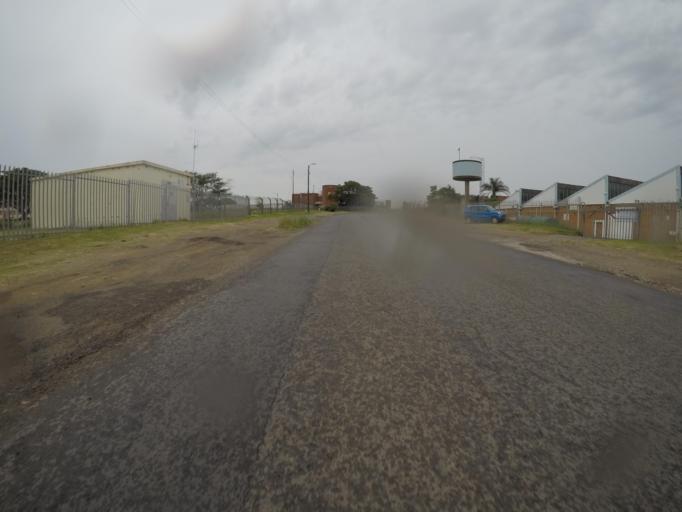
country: ZA
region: Eastern Cape
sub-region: Buffalo City Metropolitan Municipality
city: East London
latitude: -32.9733
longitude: 27.8229
